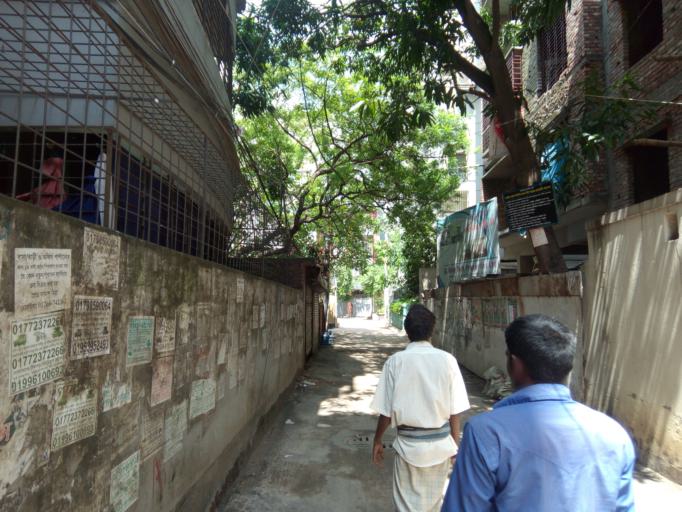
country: BD
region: Dhaka
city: Azimpur
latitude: 23.7502
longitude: 90.3818
